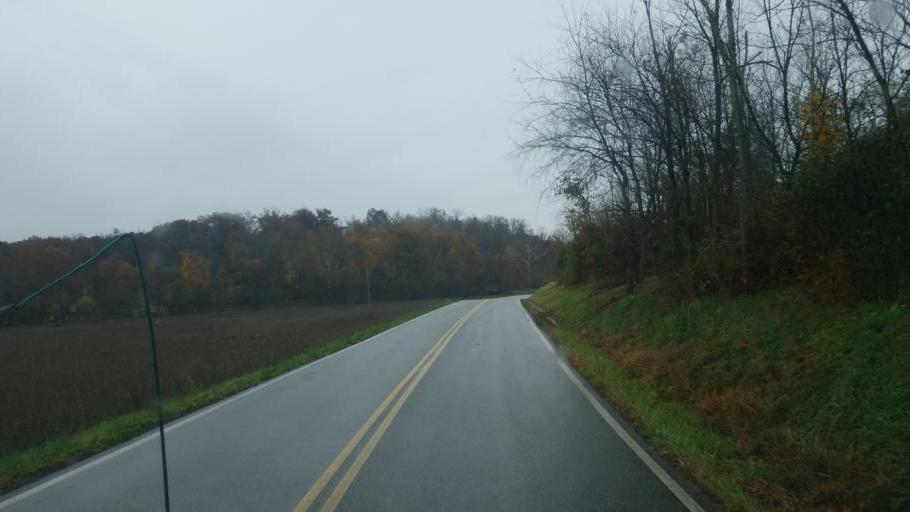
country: US
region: West Virginia
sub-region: Wood County
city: Blennerhassett
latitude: 39.3335
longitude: -81.6221
